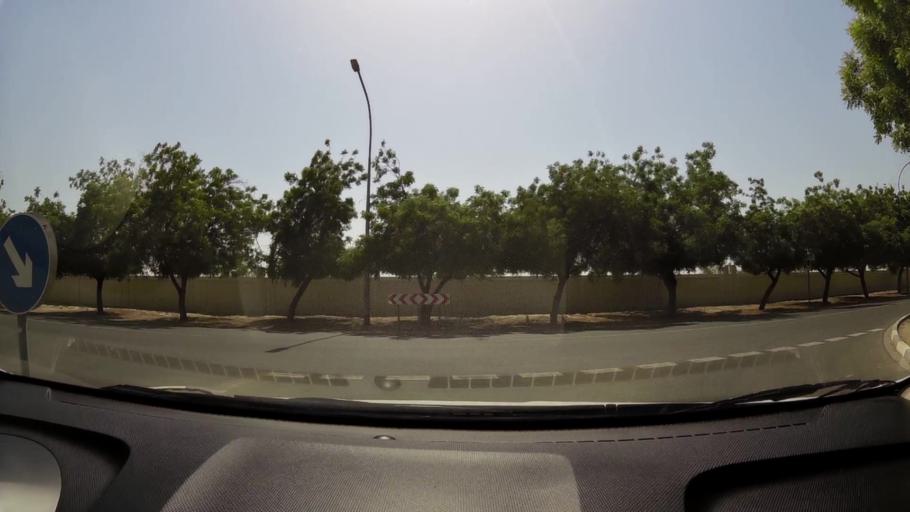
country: AE
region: Ash Shariqah
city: Sharjah
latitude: 25.2713
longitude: 55.3600
